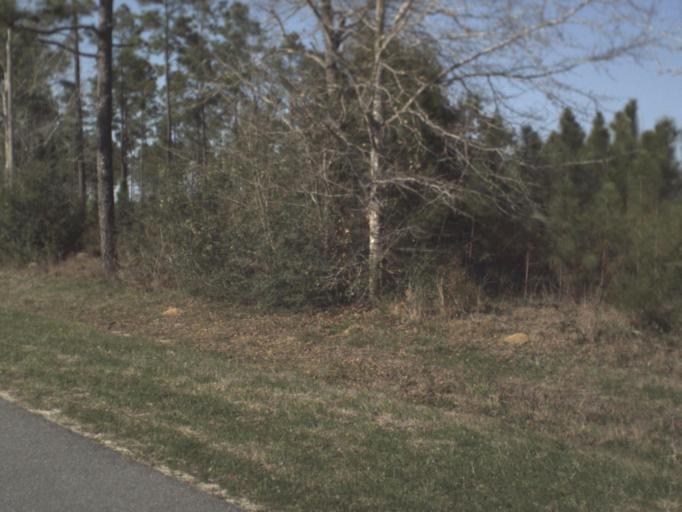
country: US
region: Florida
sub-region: Gulf County
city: Wewahitchka
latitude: 30.2457
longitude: -85.2235
